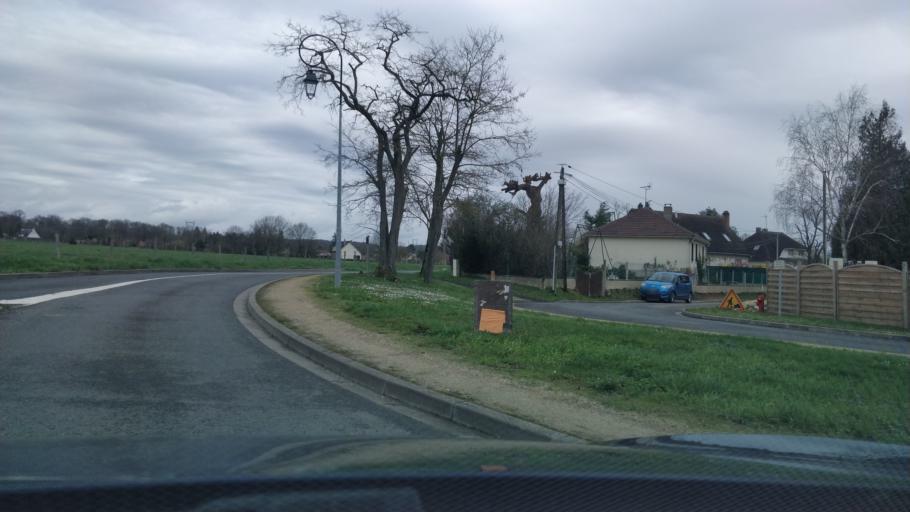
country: FR
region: Ile-de-France
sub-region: Departement de l'Essonne
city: Vaugrigneuse
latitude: 48.5964
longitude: 2.1173
